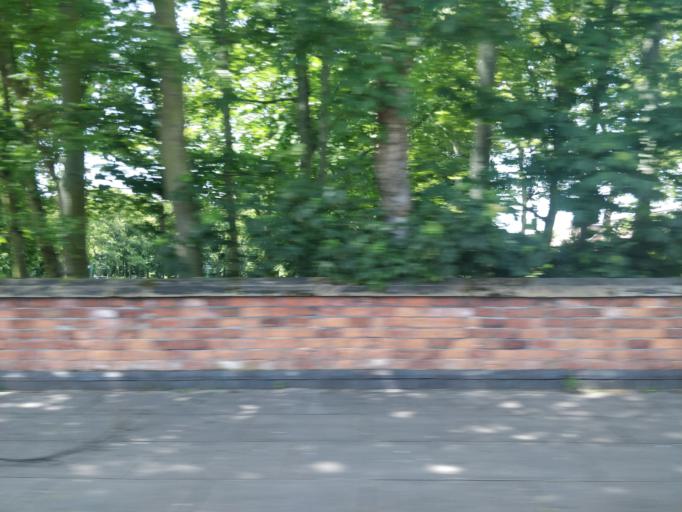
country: GB
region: England
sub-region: Lancashire
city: Banks
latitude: 53.6627
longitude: -2.9564
